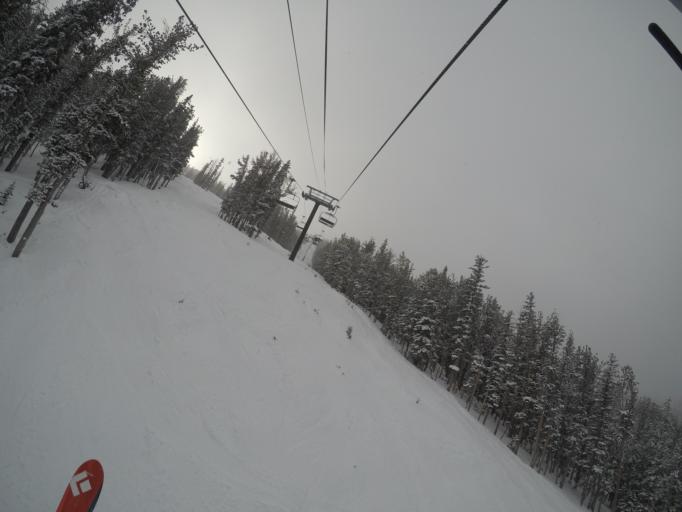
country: US
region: Montana
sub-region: Carbon County
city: Red Lodge
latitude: 45.1871
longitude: -109.3678
